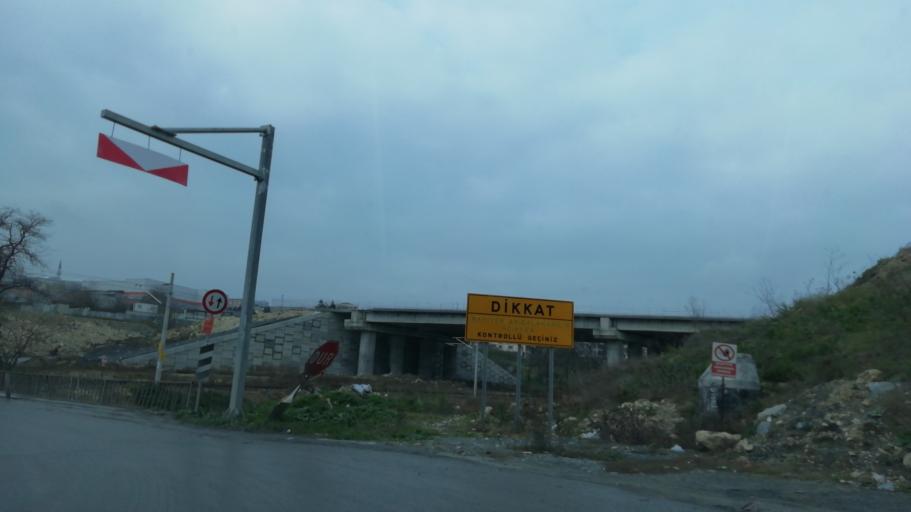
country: TR
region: Istanbul
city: Esenyurt
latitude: 41.1128
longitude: 28.6461
